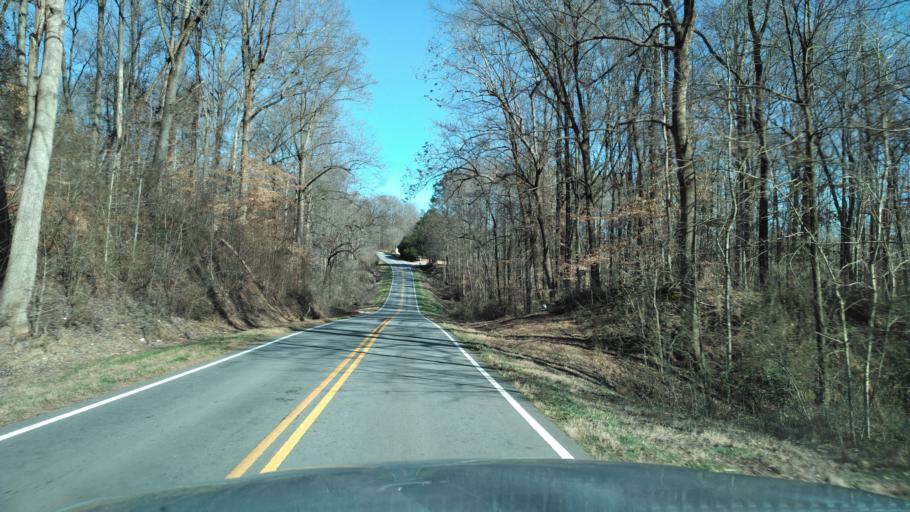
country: US
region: Georgia
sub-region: Hall County
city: Lula
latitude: 34.3117
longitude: -83.7229
